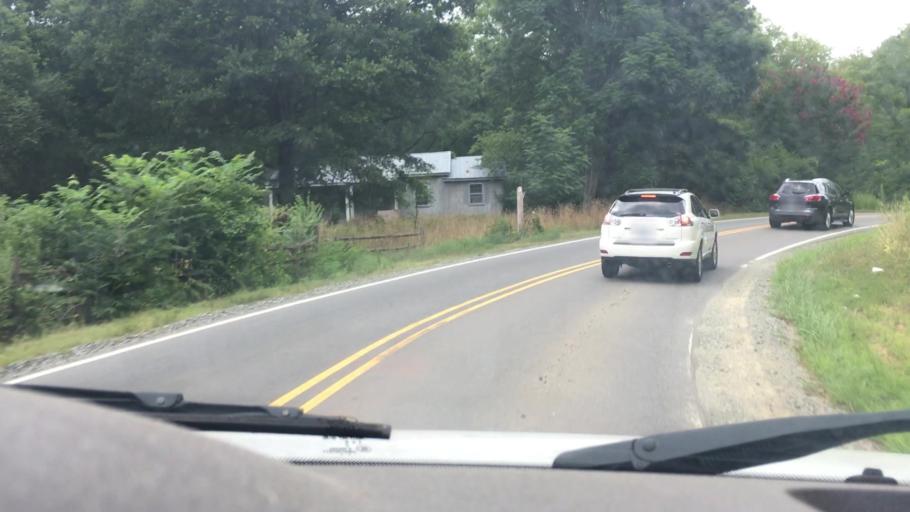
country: US
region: North Carolina
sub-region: Gaston County
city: Davidson
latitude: 35.4607
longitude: -80.7907
